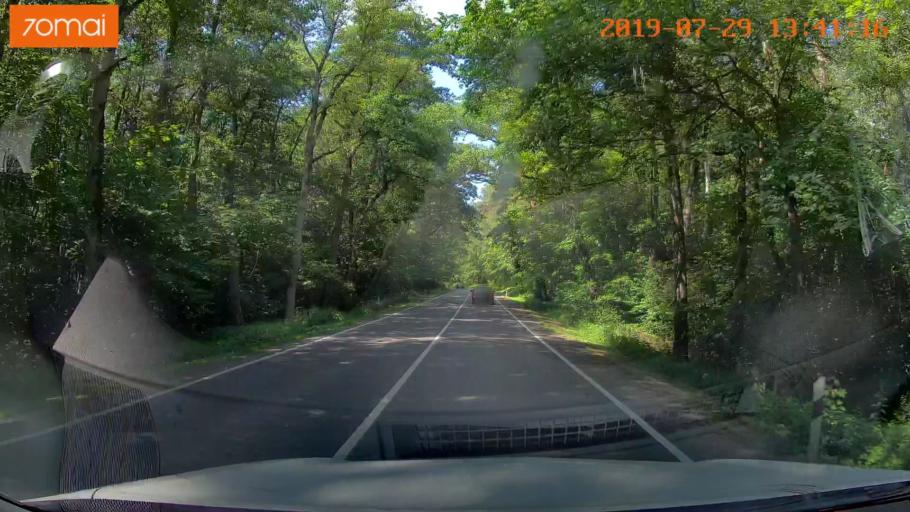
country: RU
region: Kaliningrad
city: Svetlyy
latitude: 54.7346
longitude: 20.1294
